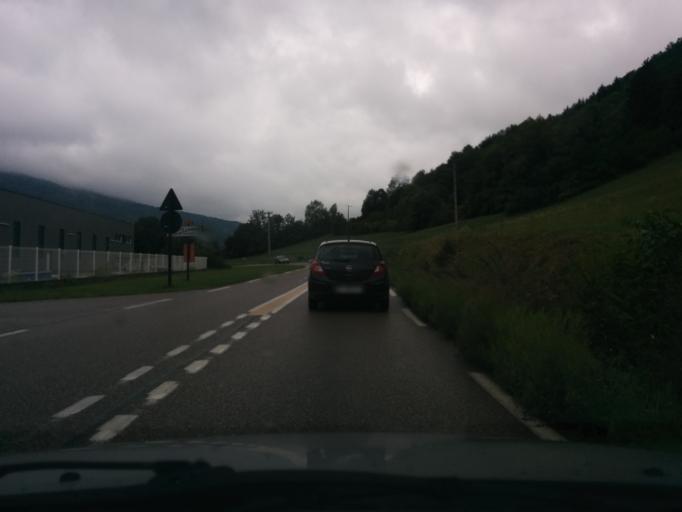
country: FR
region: Rhone-Alpes
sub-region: Departement de l'Isere
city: Saint-Geoire-en-Valdaine
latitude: 45.4418
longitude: 5.6164
